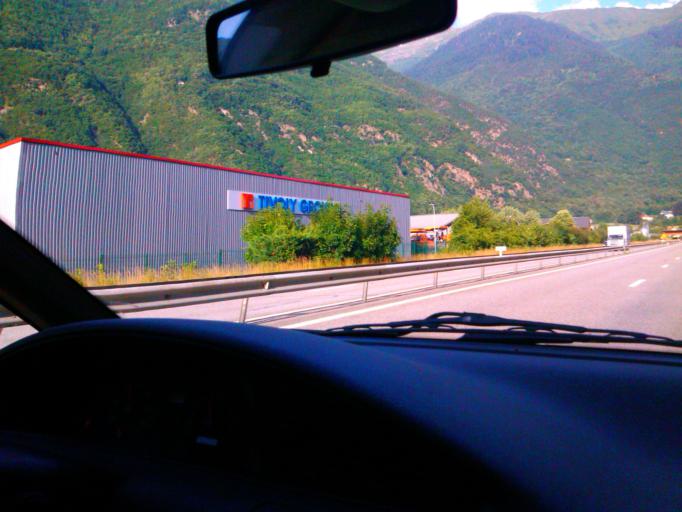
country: FR
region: Rhone-Alpes
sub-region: Departement de la Savoie
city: Albertville
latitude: 45.6597
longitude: 6.4223
